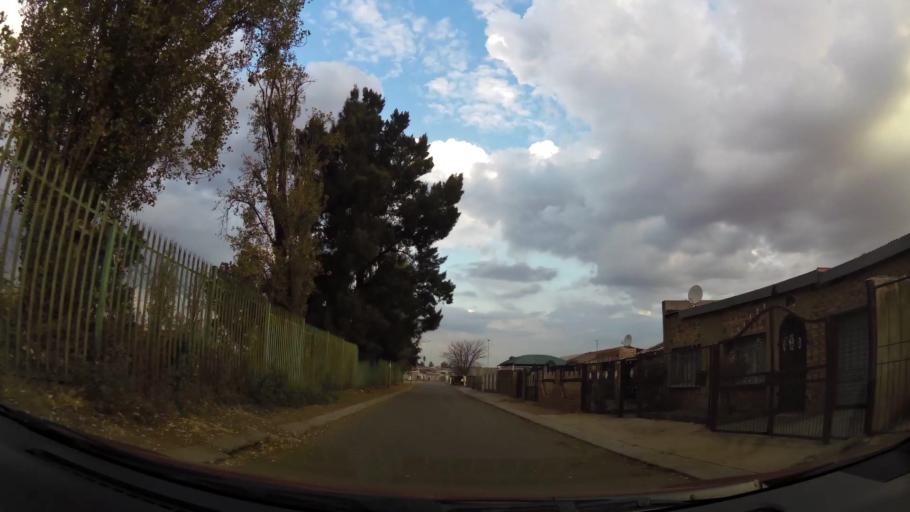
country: ZA
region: Gauteng
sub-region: City of Johannesburg Metropolitan Municipality
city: Soweto
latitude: -26.2461
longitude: 27.8248
